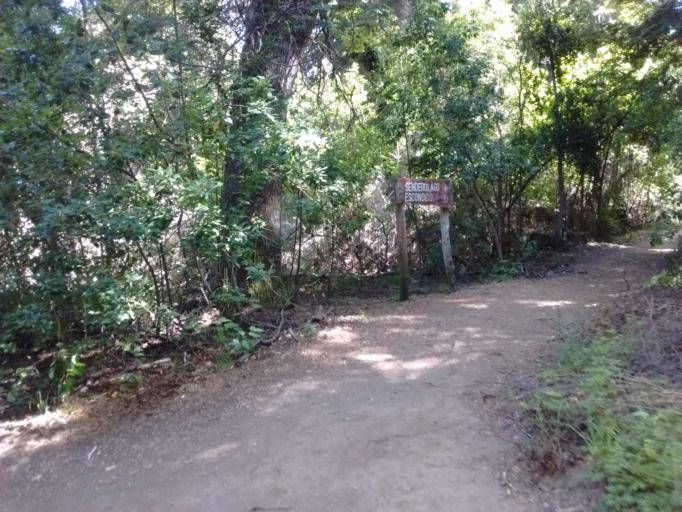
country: AR
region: Rio Negro
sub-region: Departamento de Bariloche
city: San Carlos de Bariloche
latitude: -41.0633
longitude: -71.5685
